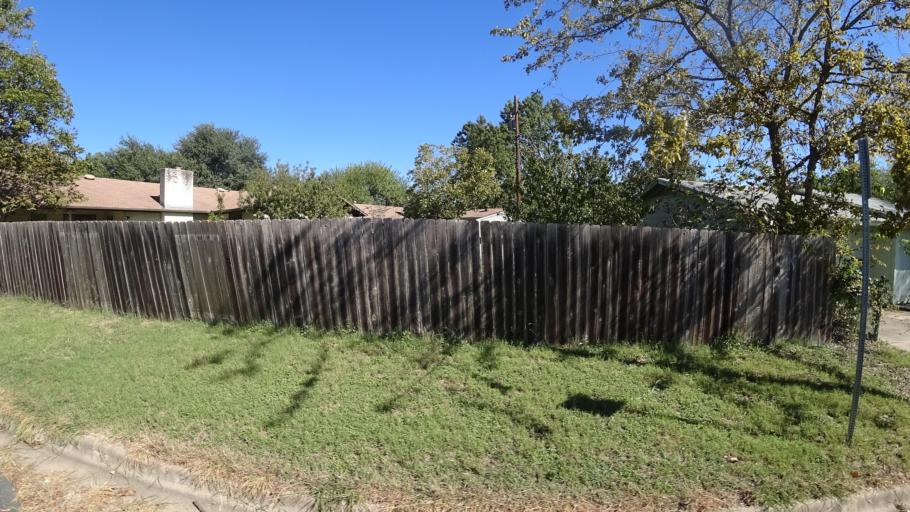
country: US
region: Texas
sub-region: Travis County
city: Austin
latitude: 30.3037
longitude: -97.6933
